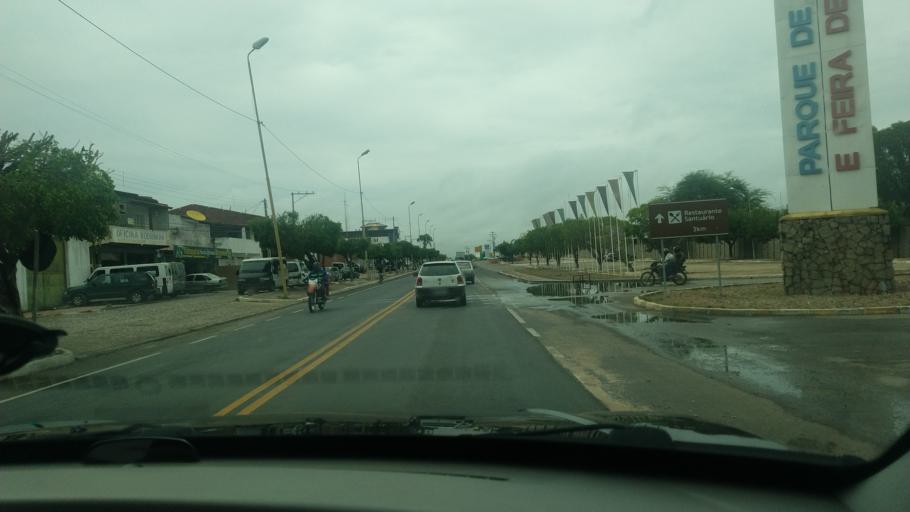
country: BR
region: Bahia
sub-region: Paulo Afonso
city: Paulo Afonso
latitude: -9.4078
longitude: -38.2368
